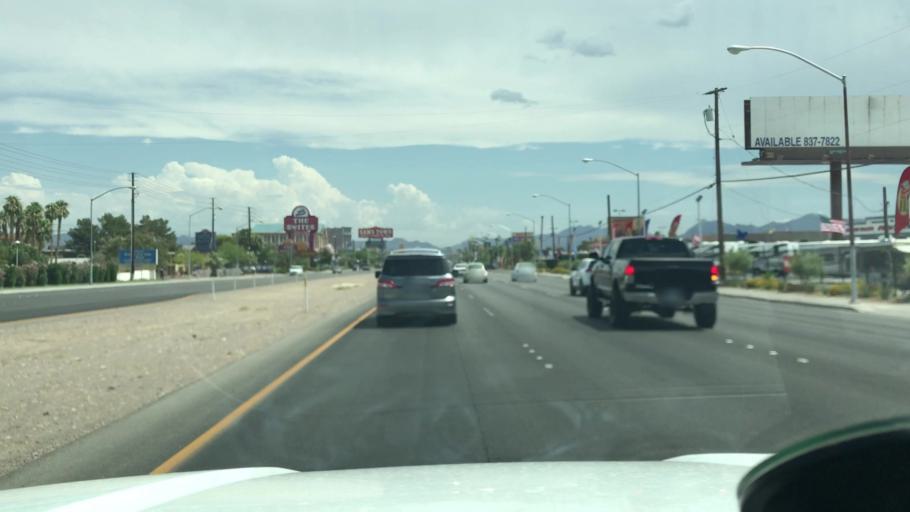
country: US
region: Nevada
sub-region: Clark County
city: Whitney
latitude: 36.1181
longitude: -115.0705
